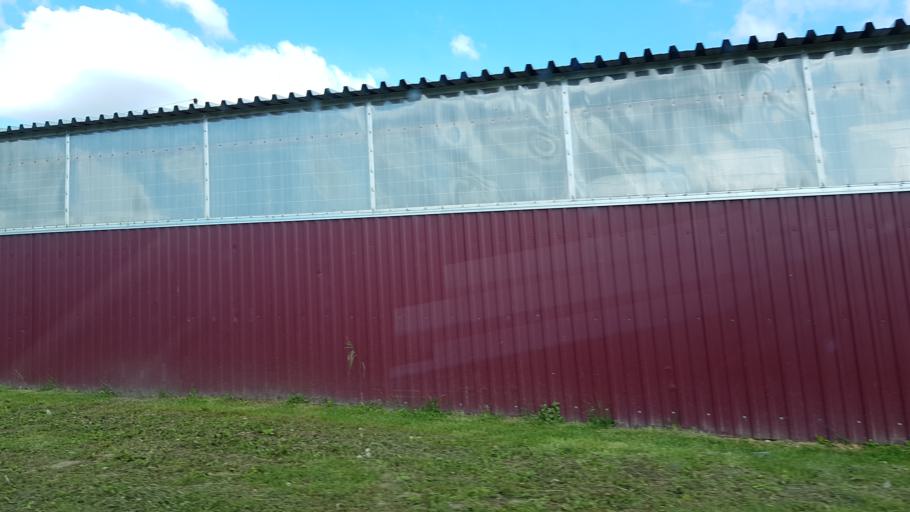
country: BY
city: Fanipol
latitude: 53.7683
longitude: 27.3407
